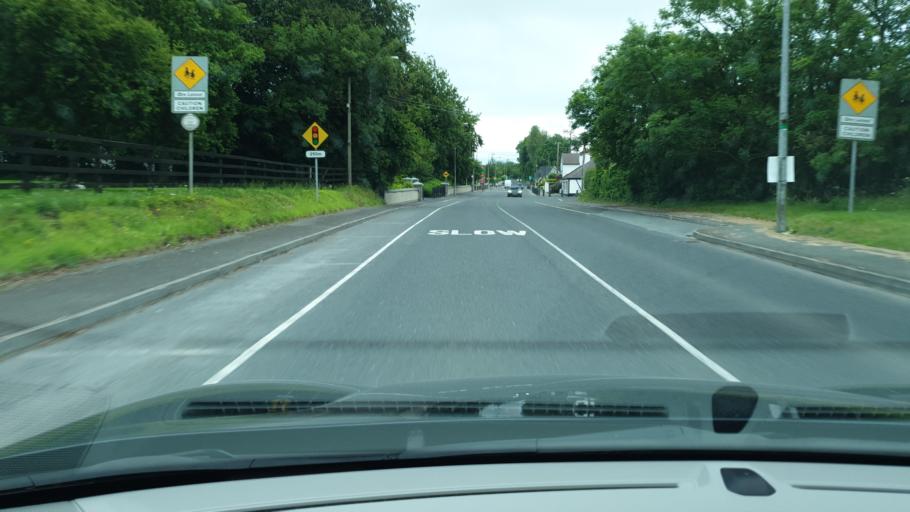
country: IE
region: Leinster
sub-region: An Mhi
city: Dunshaughlin
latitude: 53.4702
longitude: -6.5379
